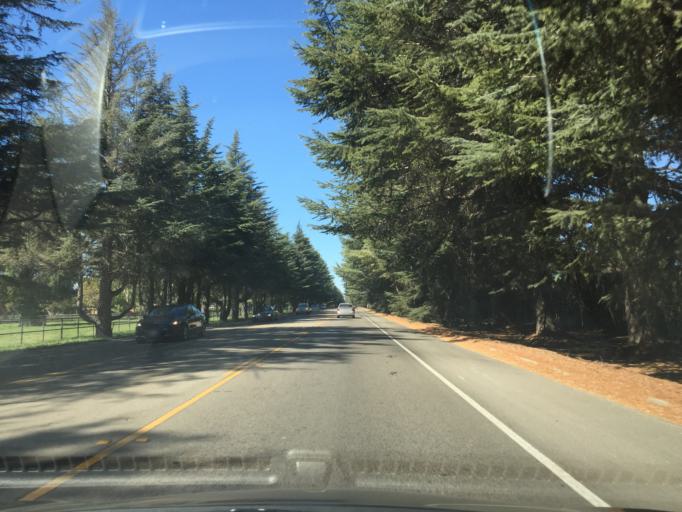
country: US
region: California
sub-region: Santa Barbara County
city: Solvang
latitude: 34.6012
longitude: -120.1643
